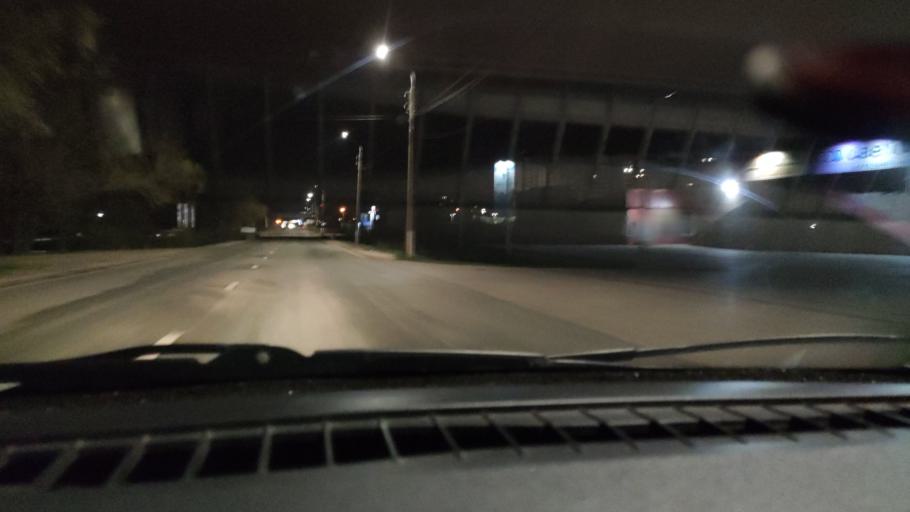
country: RU
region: Bashkortostan
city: Sterlitamak
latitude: 53.6432
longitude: 55.8939
